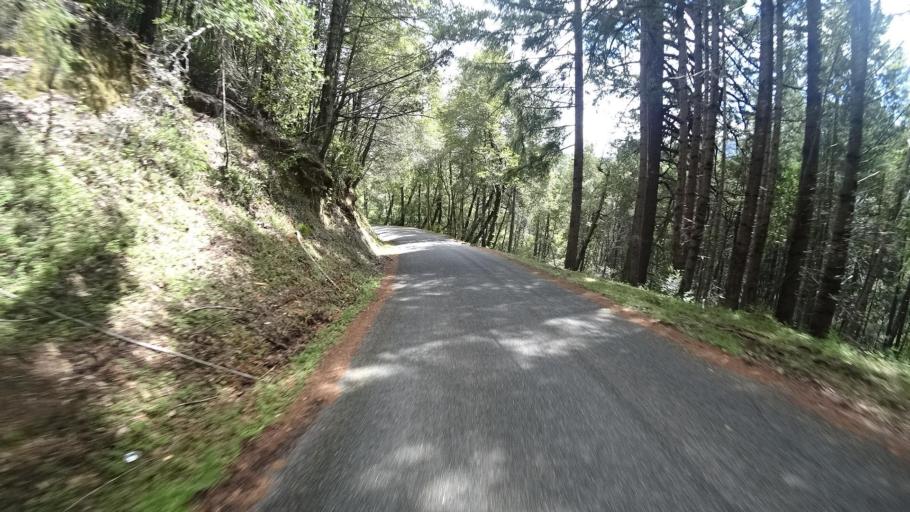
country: US
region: California
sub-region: Humboldt County
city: Blue Lake
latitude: 40.7588
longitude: -123.9212
